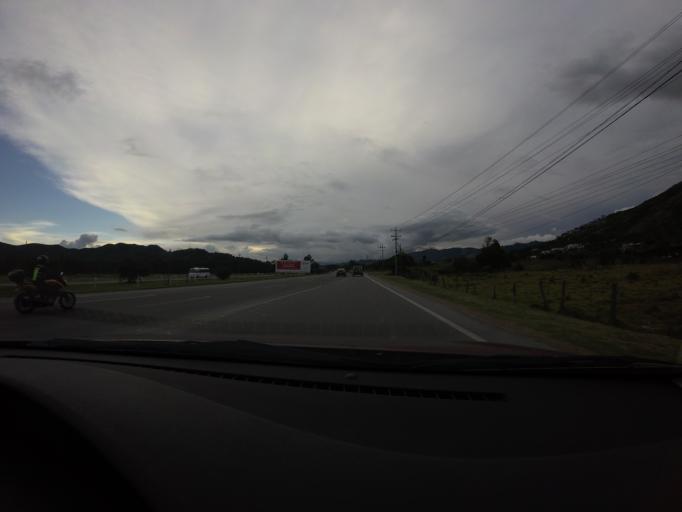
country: CO
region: Cundinamarca
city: Sopo
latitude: 4.9396
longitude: -73.9677
